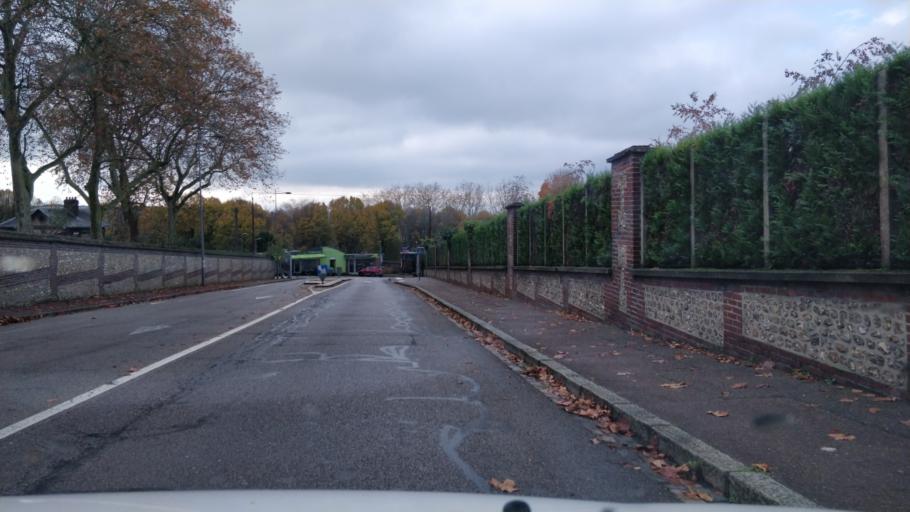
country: FR
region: Haute-Normandie
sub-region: Departement de la Seine-Maritime
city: Bihorel
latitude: 49.4499
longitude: 1.1208
